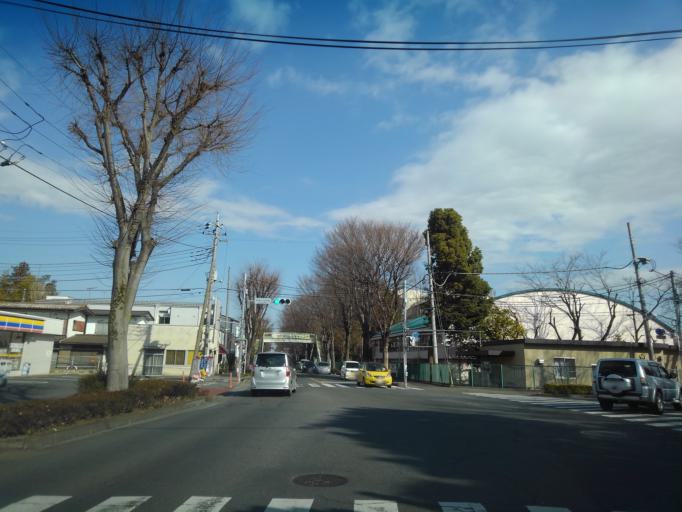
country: JP
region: Saitama
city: Tokorozawa
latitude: 35.8081
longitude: 139.4614
